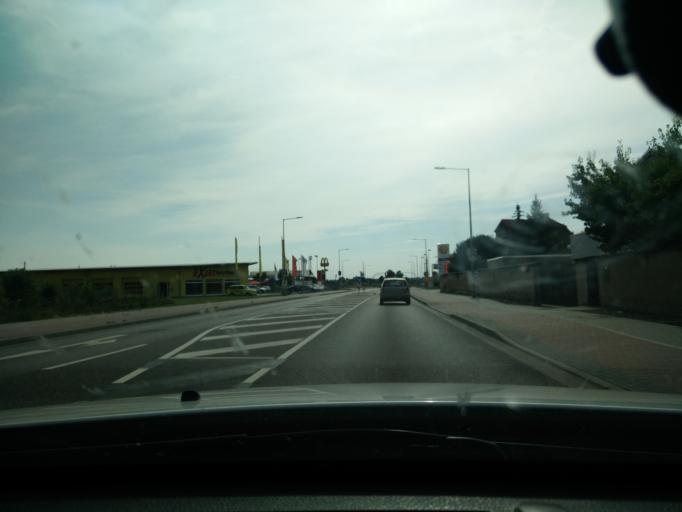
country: DE
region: Saxony-Anhalt
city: Burg bei Magdeburg
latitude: 52.2602
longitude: 11.8434
